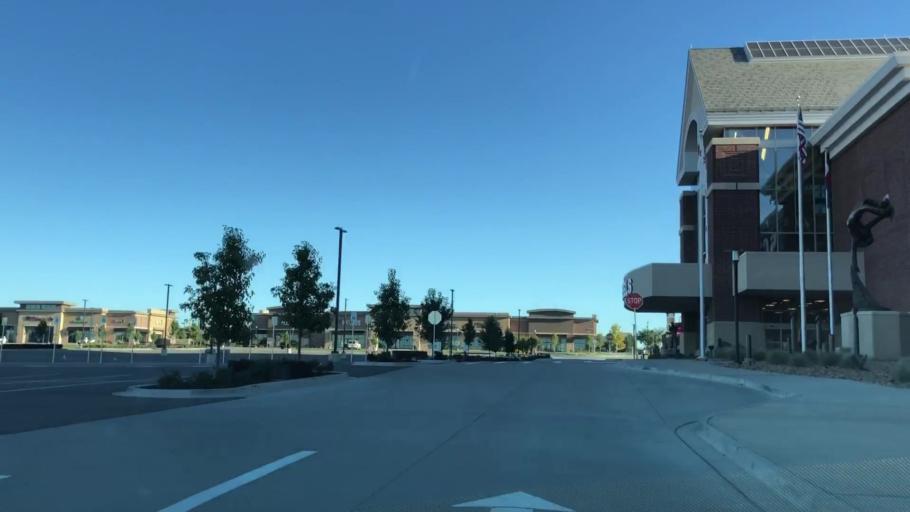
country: US
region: Colorado
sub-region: Larimer County
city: Loveland
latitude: 40.4038
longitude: -104.9802
